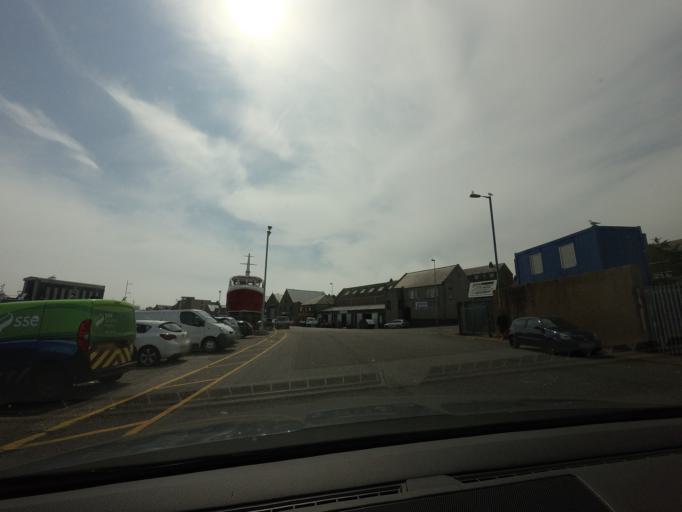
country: GB
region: Scotland
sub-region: Aberdeenshire
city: Peterhead
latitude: 57.5071
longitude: -1.7756
